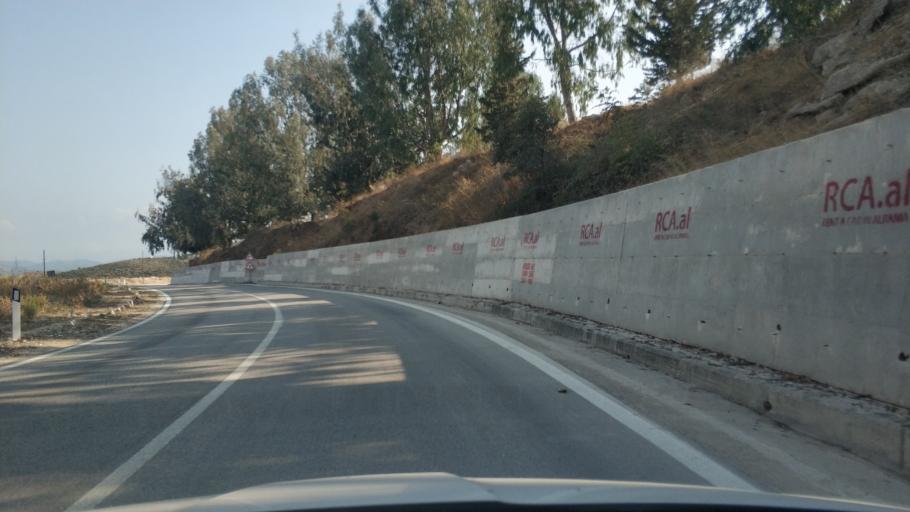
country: AL
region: Vlore
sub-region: Rrethi i Sarandes
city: Sarande
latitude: 39.8889
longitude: 20.0165
